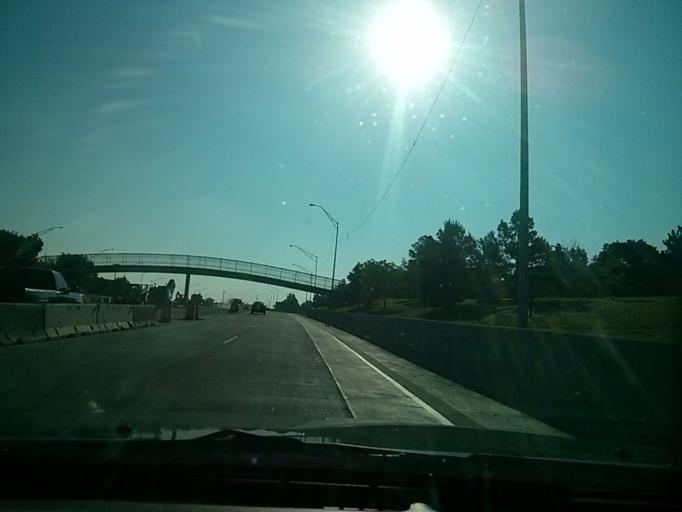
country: US
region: Oklahoma
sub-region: Tulsa County
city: Tulsa
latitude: 36.1602
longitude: -95.9554
